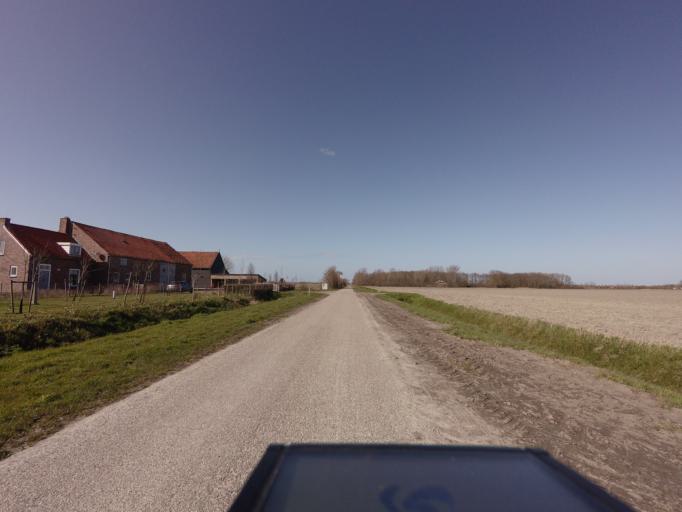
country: NL
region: Zeeland
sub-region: Schouwen-Duiveland
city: Scharendijke
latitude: 51.7114
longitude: 3.8186
